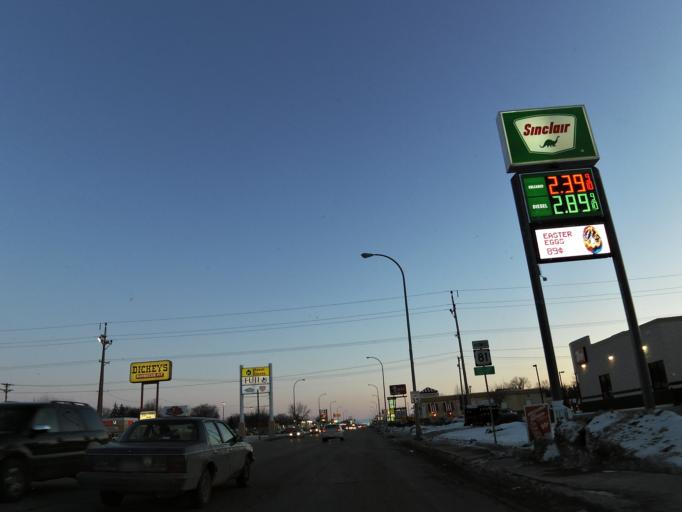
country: US
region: North Dakota
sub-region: Grand Forks County
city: Grand Forks
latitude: 47.9160
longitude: -97.0451
